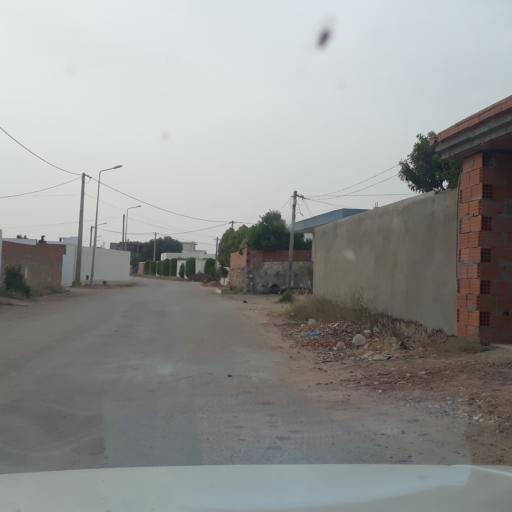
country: TN
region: Safaqis
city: Al Qarmadah
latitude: 34.8197
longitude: 10.7766
